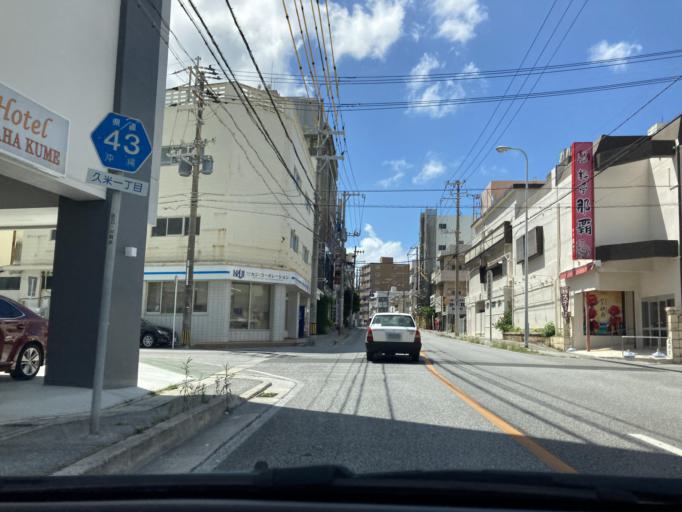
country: JP
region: Okinawa
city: Naha-shi
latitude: 26.2178
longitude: 127.6730
